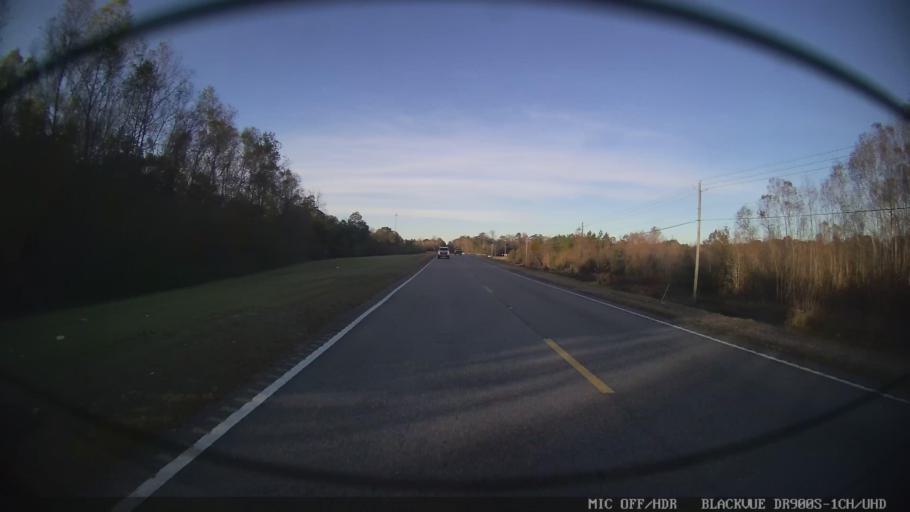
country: US
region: Mississippi
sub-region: Lamar County
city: Lumberton
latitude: 31.0078
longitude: -89.4505
